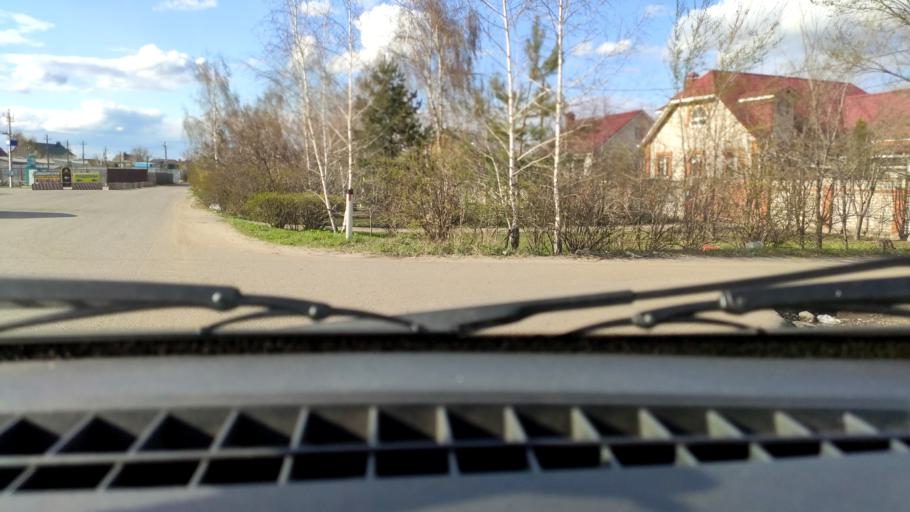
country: RU
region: Voronezj
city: Somovo
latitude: 51.6782
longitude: 39.3191
